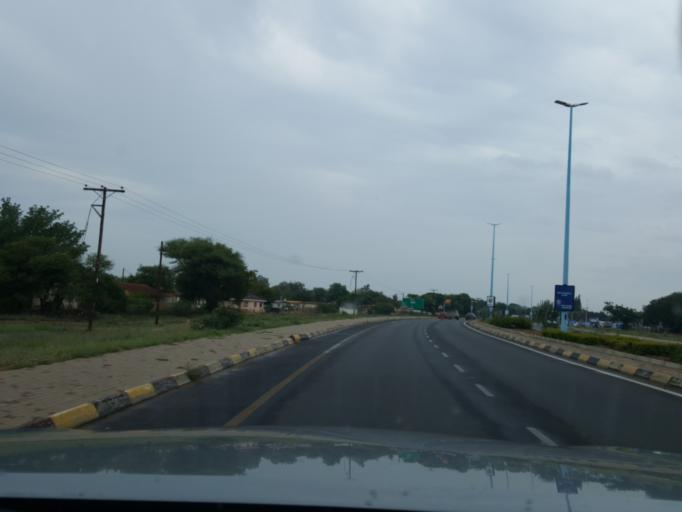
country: BW
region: South East
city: Gaborone
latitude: -24.6197
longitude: 25.9312
